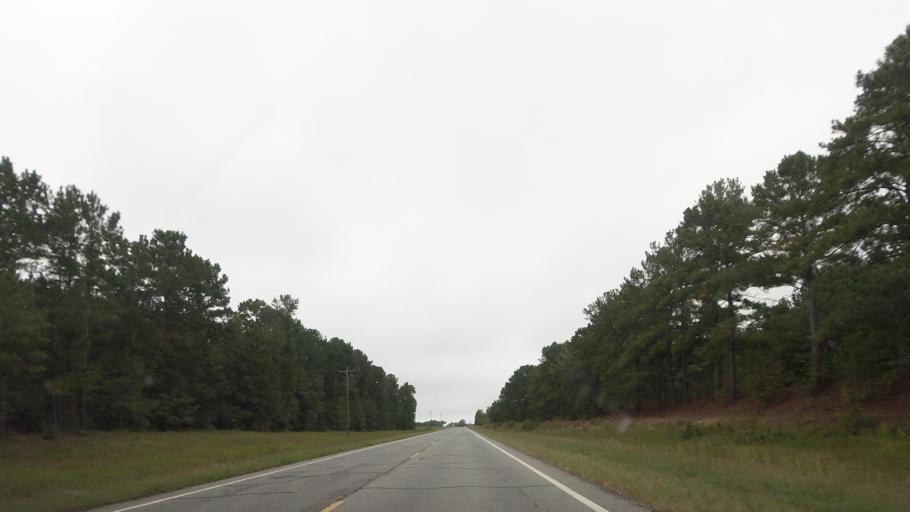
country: US
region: Georgia
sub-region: Irwin County
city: Ocilla
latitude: 31.5026
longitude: -83.2388
